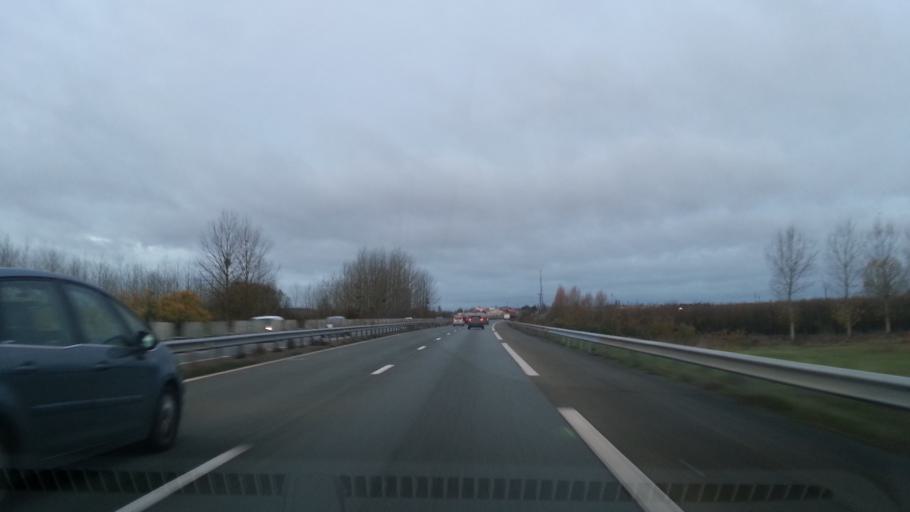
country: FR
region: Picardie
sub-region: Departement de l'Oise
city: Bresles
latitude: 49.4144
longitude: 2.2693
